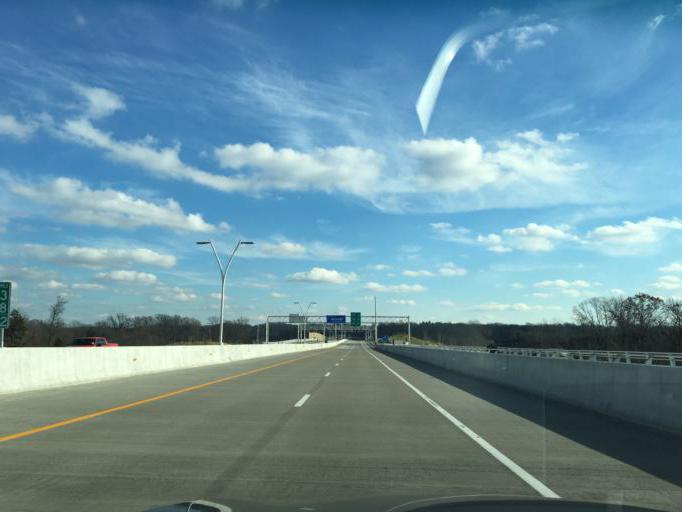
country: US
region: Kentucky
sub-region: Jefferson County
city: Prospect
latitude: 38.3369
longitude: -85.6366
